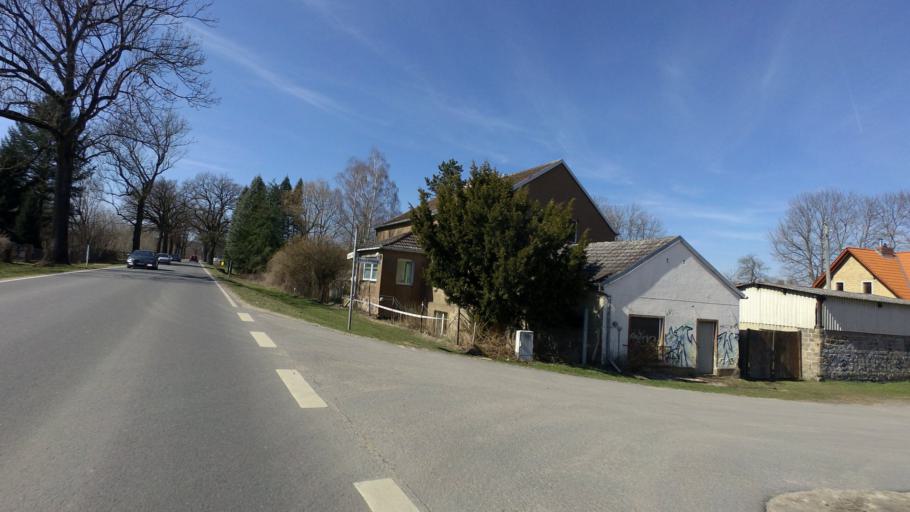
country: DE
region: Brandenburg
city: Waldsieversdorf
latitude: 52.5238
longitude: 14.0946
